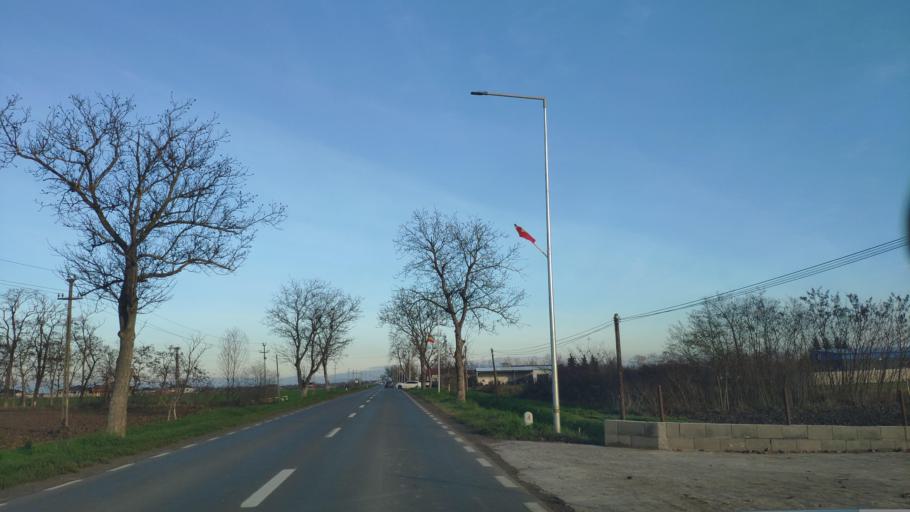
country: RO
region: Satu Mare
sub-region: Comuna Paulesti
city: Paulesti
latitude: 47.7974
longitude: 22.9444
